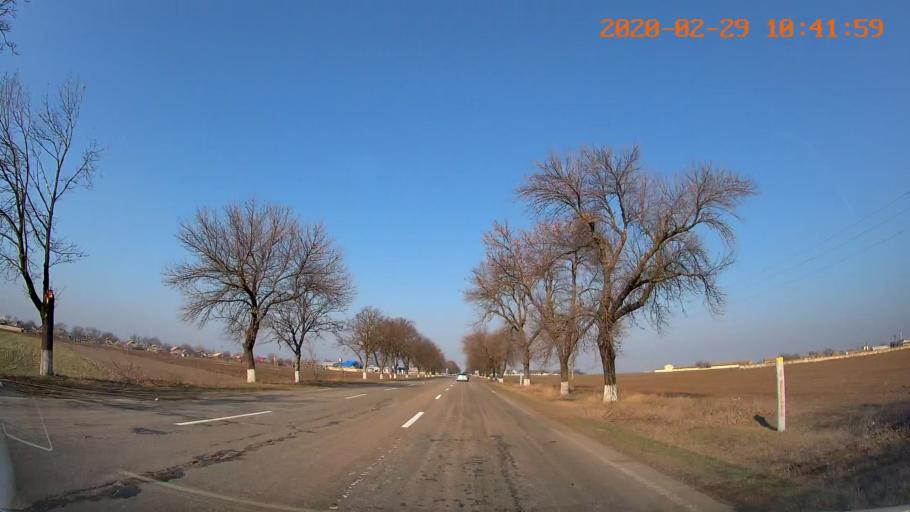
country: MD
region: Telenesti
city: Grigoriopol
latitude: 47.0476
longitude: 29.4172
